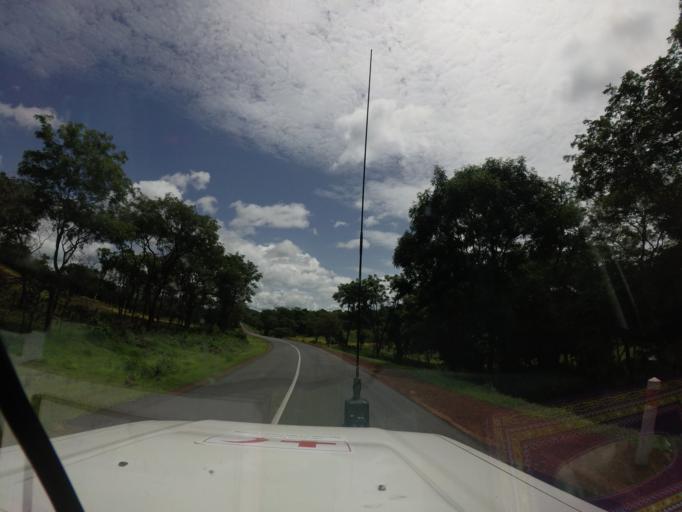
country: SL
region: Northern Province
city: Gberia Fotombu
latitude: 10.1768
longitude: -11.2033
